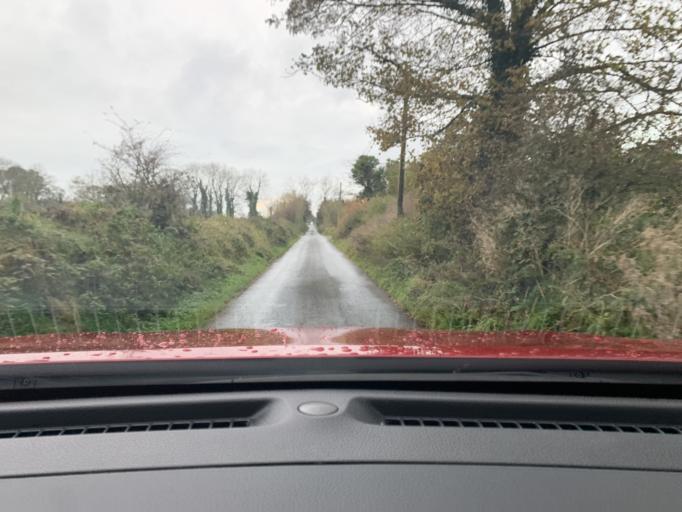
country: IE
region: Connaught
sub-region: Roscommon
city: Ballaghaderreen
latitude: 53.9666
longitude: -8.5651
